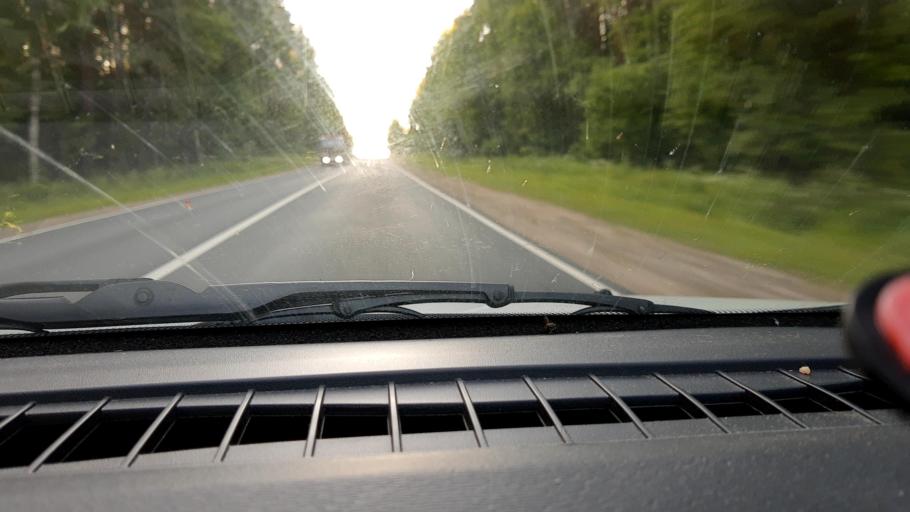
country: RU
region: Nizjnij Novgorod
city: Krasnyye Baki
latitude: 56.9969
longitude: 45.1137
